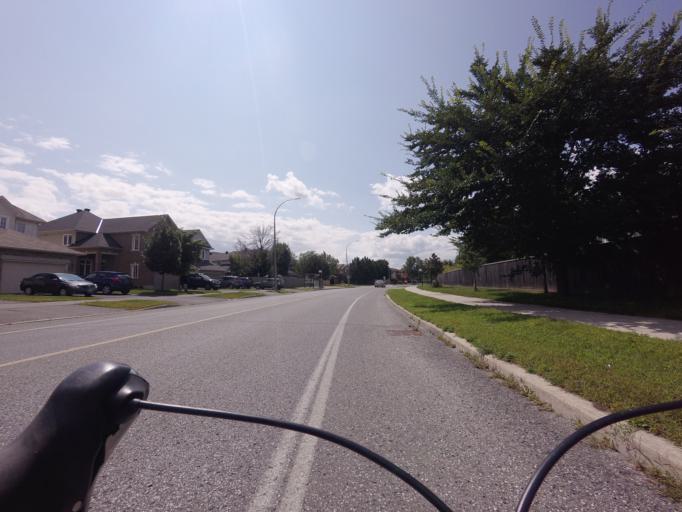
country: CA
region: Ontario
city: Bells Corners
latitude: 45.2796
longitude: -75.8555
